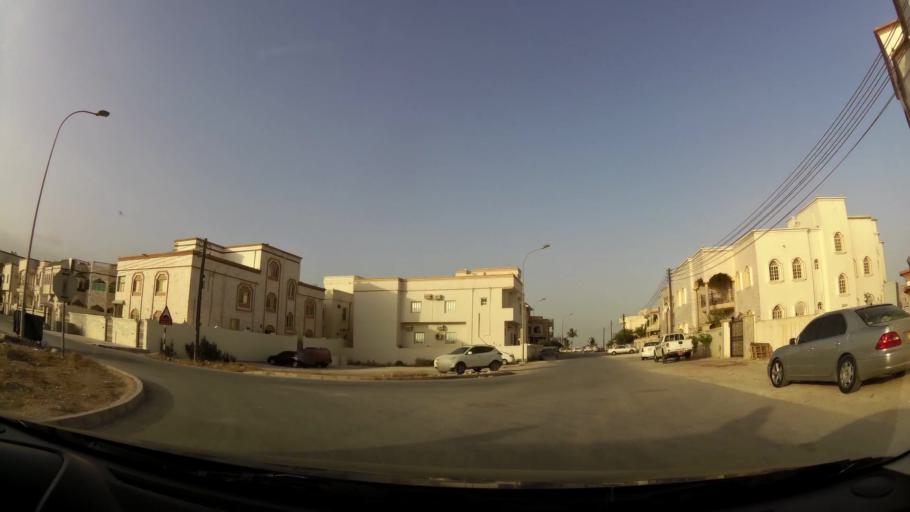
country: OM
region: Zufar
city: Salalah
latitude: 17.0158
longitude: 54.0337
